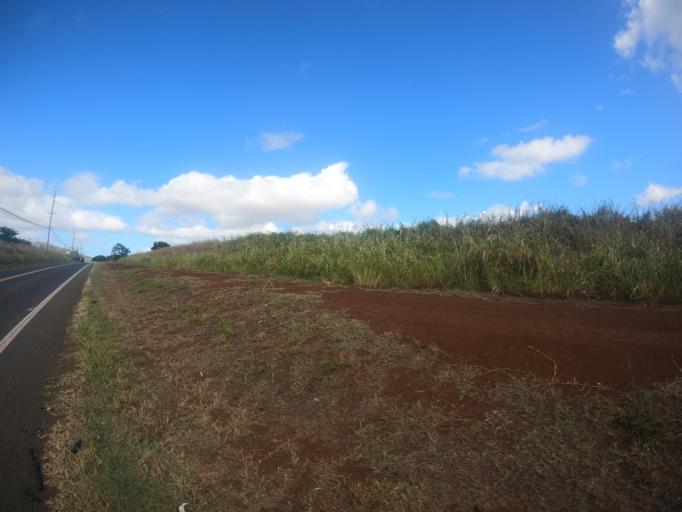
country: US
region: Hawaii
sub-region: Honolulu County
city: Village Park
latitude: 21.4308
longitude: -158.0564
